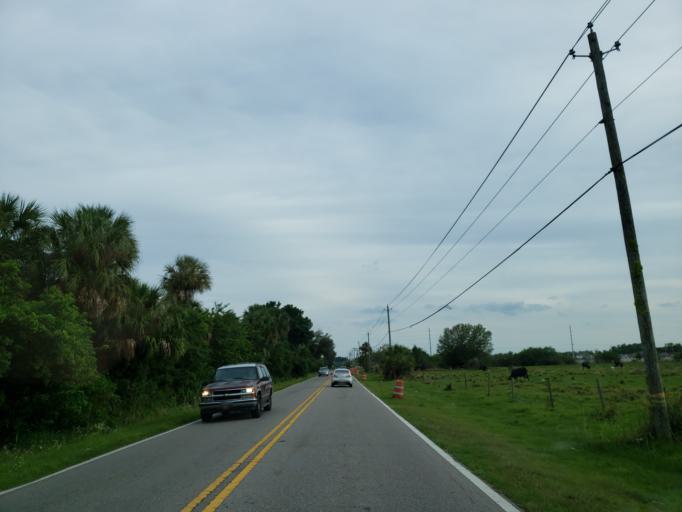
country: US
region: Florida
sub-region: Hillsborough County
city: Ruskin
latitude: 27.7378
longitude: -82.4187
